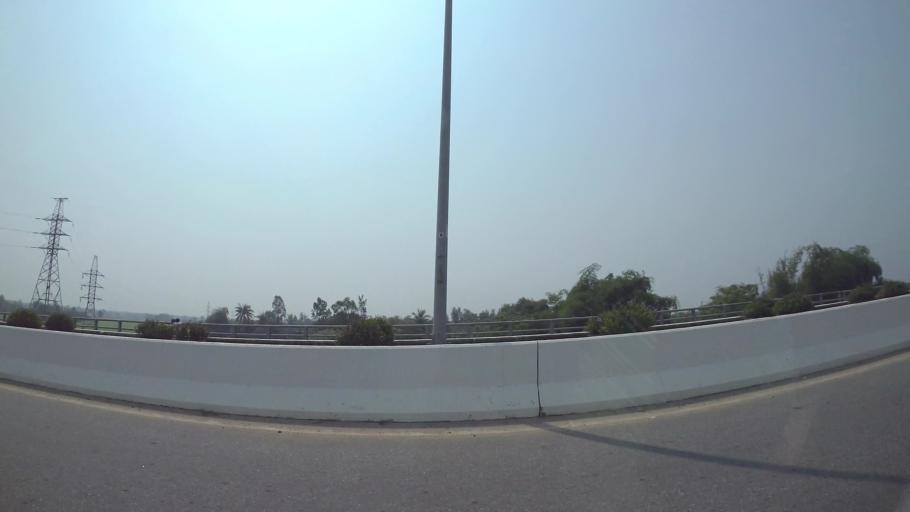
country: VN
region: Da Nang
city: Cam Le
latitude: 15.9694
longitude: 108.2183
